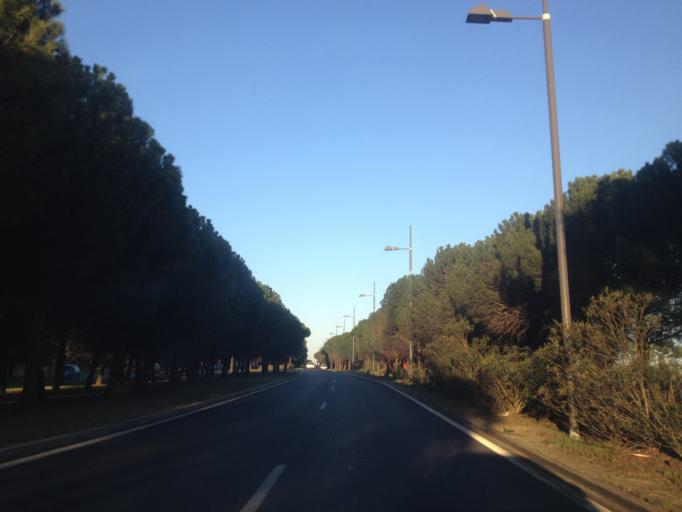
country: FR
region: Languedoc-Roussillon
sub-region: Departement de l'Herault
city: Castelnau-le-Lez
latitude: 43.6072
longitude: 3.9212
